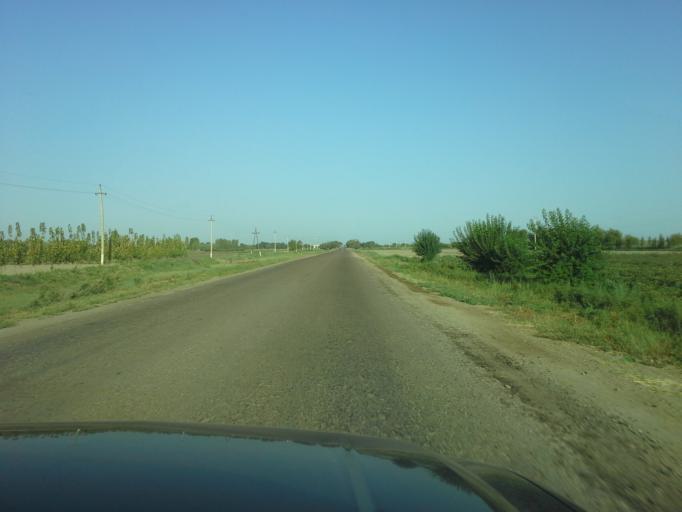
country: TM
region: Dasoguz
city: Boldumsaz
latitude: 42.2145
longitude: 59.5051
